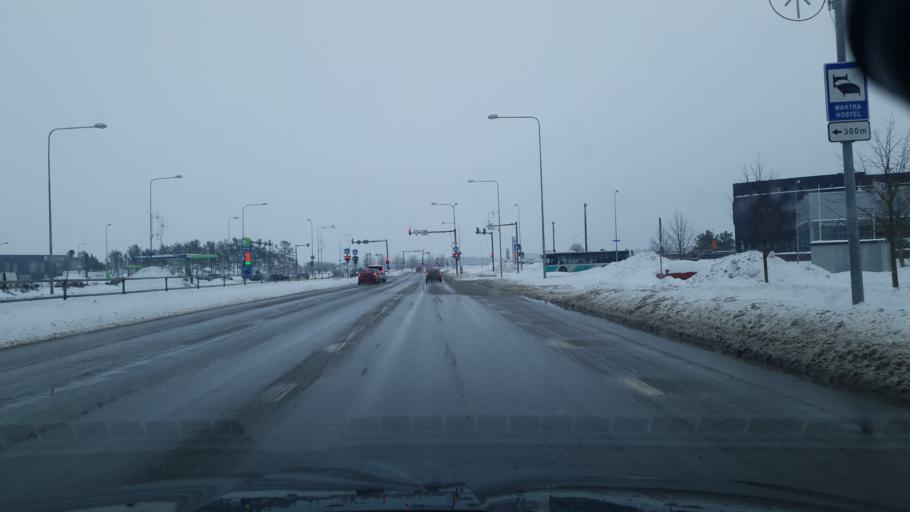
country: EE
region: Harju
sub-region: Tallinna linn
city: Kose
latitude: 59.4379
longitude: 24.8716
